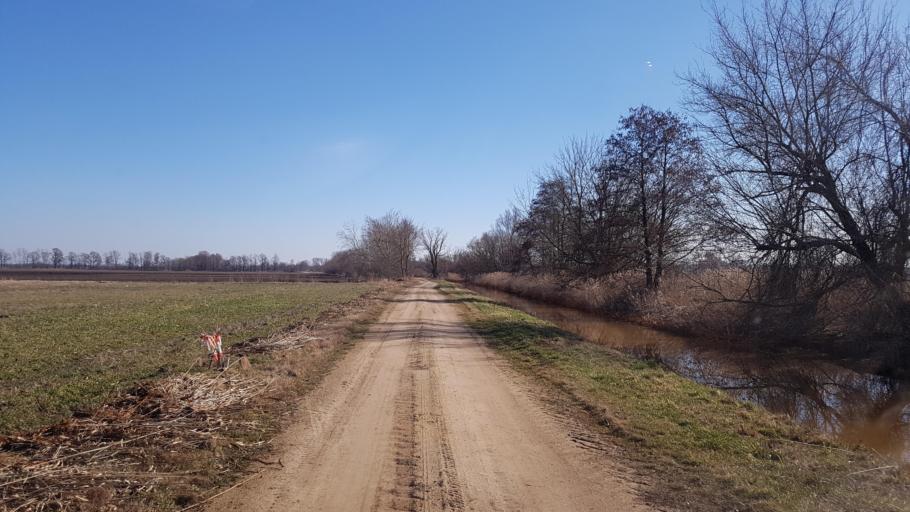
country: DE
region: Brandenburg
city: Hirschfeld
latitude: 51.4142
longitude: 13.6375
